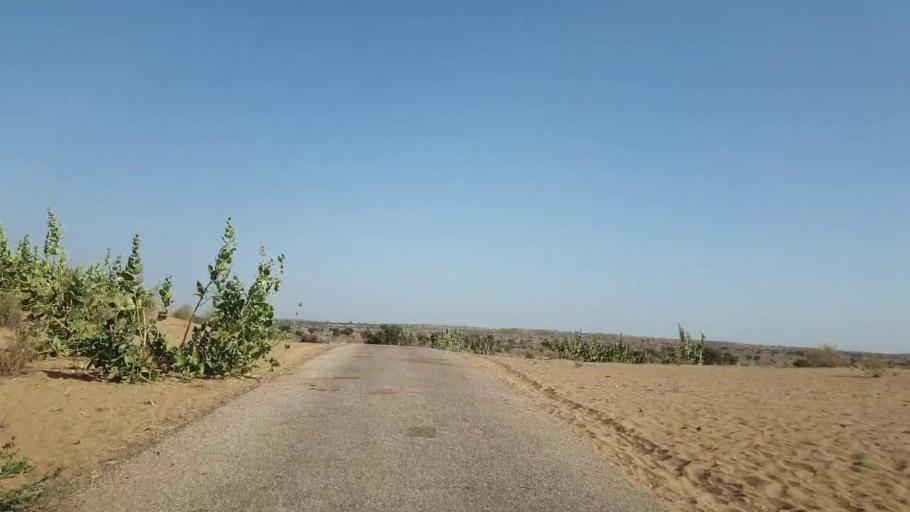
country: PK
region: Sindh
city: Islamkot
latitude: 25.0361
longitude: 70.0281
